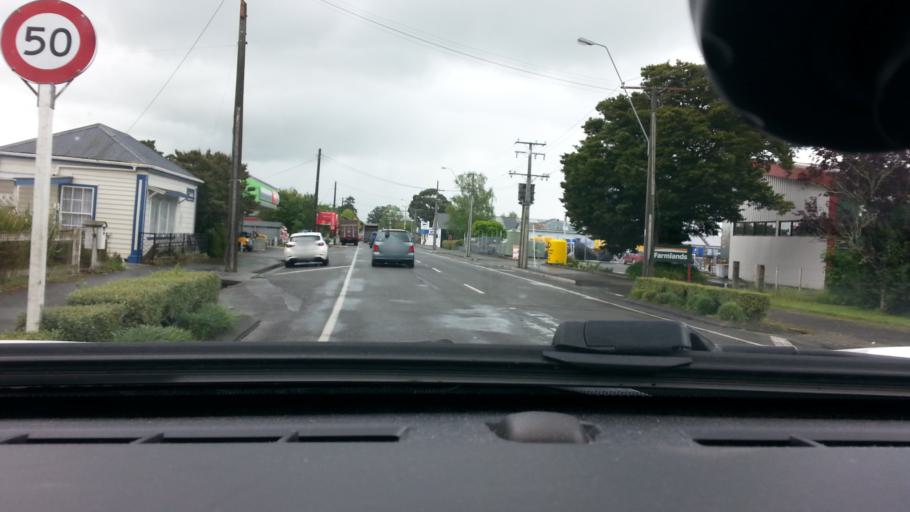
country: NZ
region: Wellington
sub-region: Masterton District
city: Masterton
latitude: -41.0886
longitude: 175.4512
